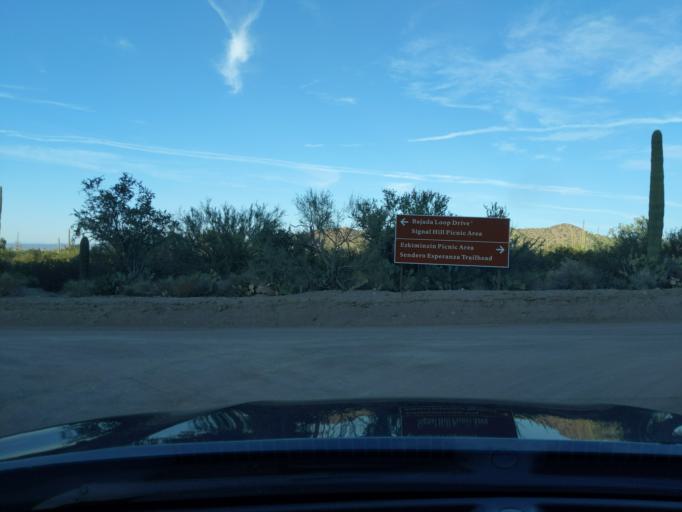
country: US
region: Arizona
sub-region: Pima County
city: Picture Rocks
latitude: 32.2857
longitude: -111.1874
